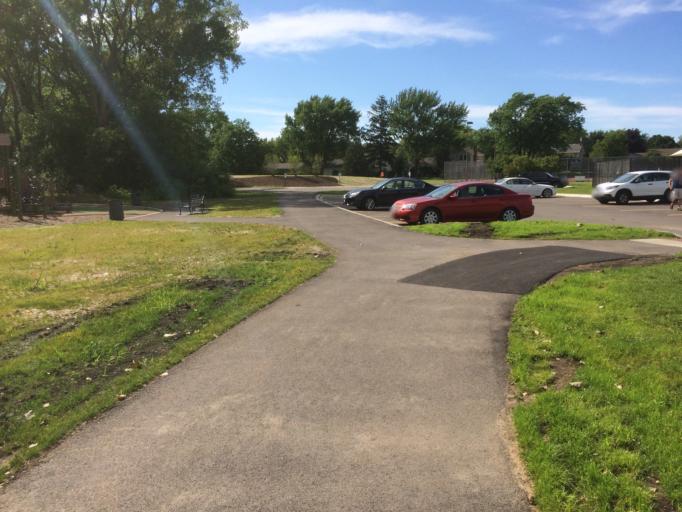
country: US
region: Illinois
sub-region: Cook County
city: Buffalo Grove
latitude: 42.1626
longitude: -87.9708
